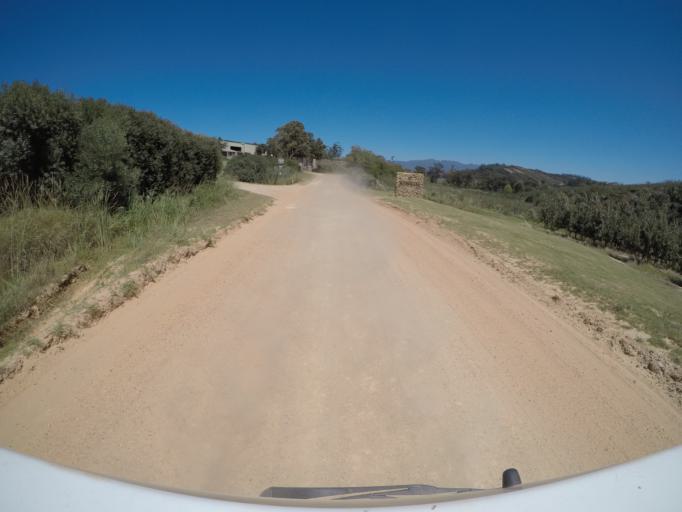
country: ZA
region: Western Cape
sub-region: Overberg District Municipality
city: Grabouw
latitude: -34.2452
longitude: 19.1017
